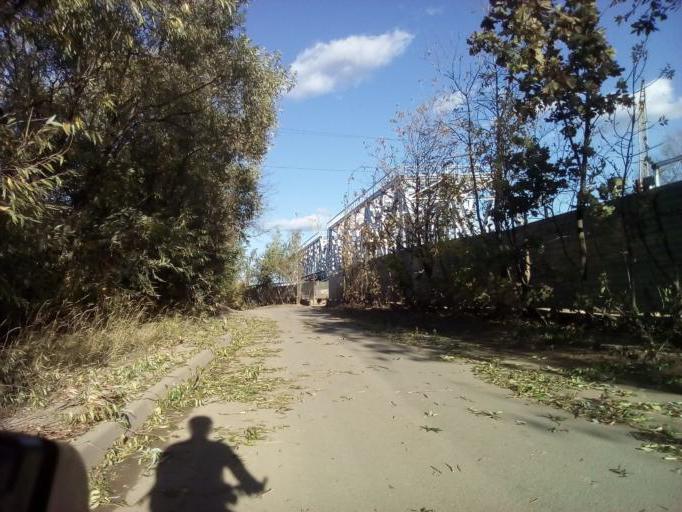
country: RU
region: Moscow
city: Likhobory
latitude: 55.8480
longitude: 37.5527
